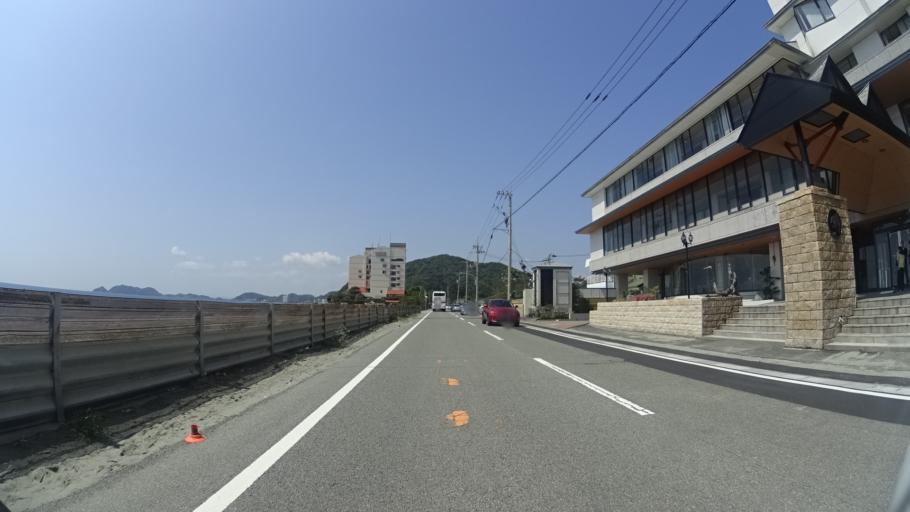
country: JP
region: Tokushima
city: Narutocho-mitsuishi
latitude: 34.2225
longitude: 134.6349
